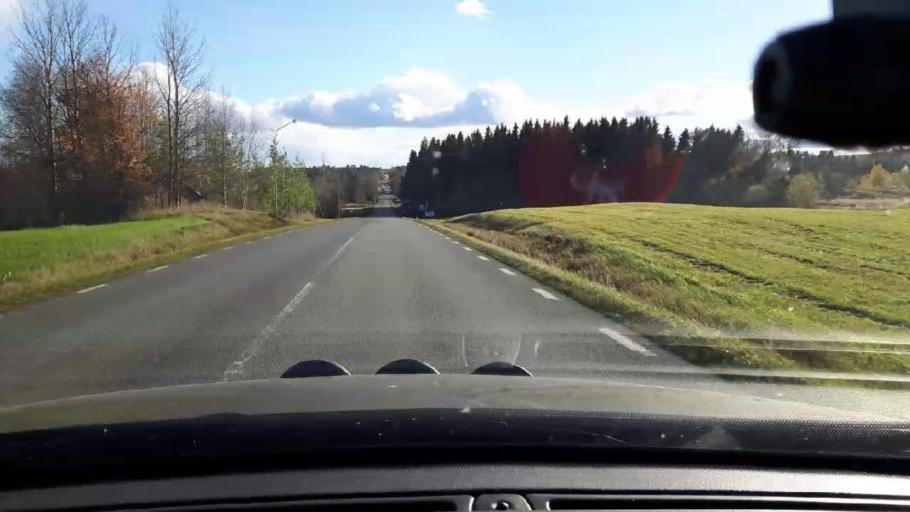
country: SE
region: Jaemtland
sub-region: Bergs Kommun
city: Hoverberg
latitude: 63.0054
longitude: 14.3400
